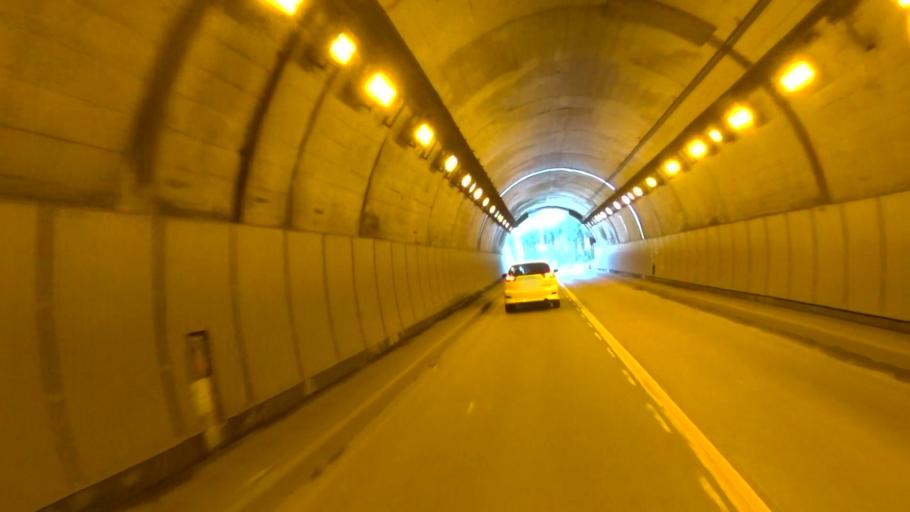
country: JP
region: Kyoto
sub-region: Kyoto-shi
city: Kamigyo-ku
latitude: 35.1143
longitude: 135.6652
